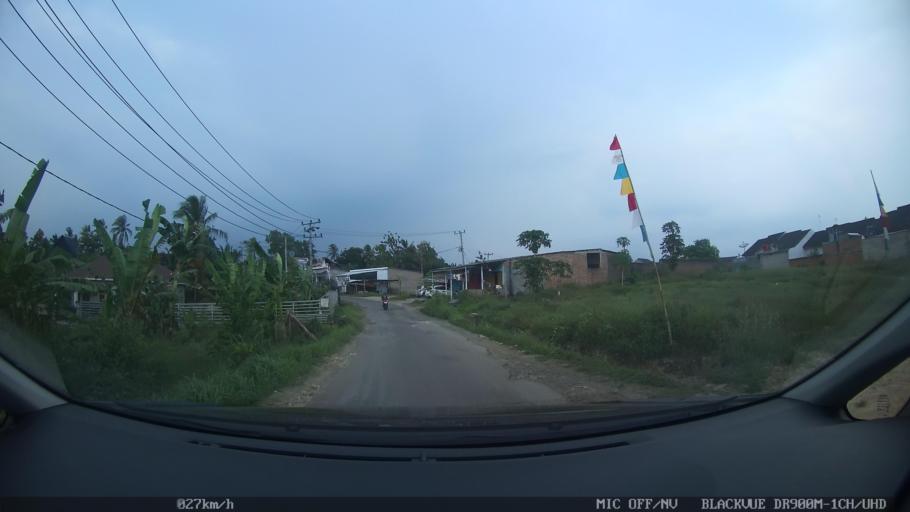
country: ID
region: Lampung
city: Kedaton
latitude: -5.3478
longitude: 105.2320
